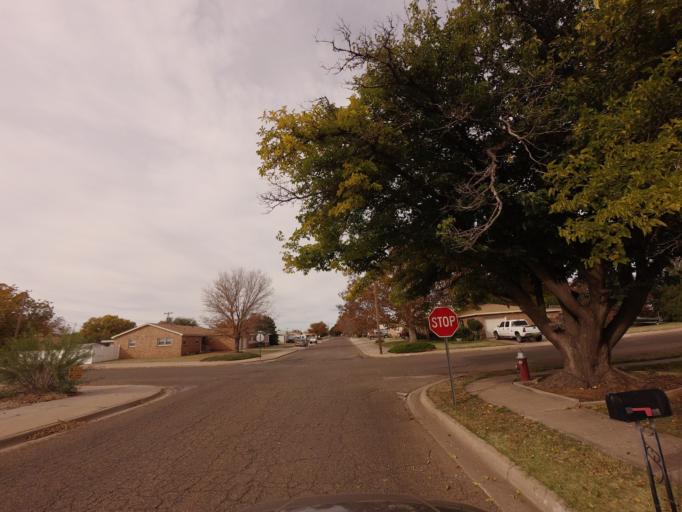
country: US
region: New Mexico
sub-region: Curry County
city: Clovis
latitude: 34.4230
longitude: -103.2112
